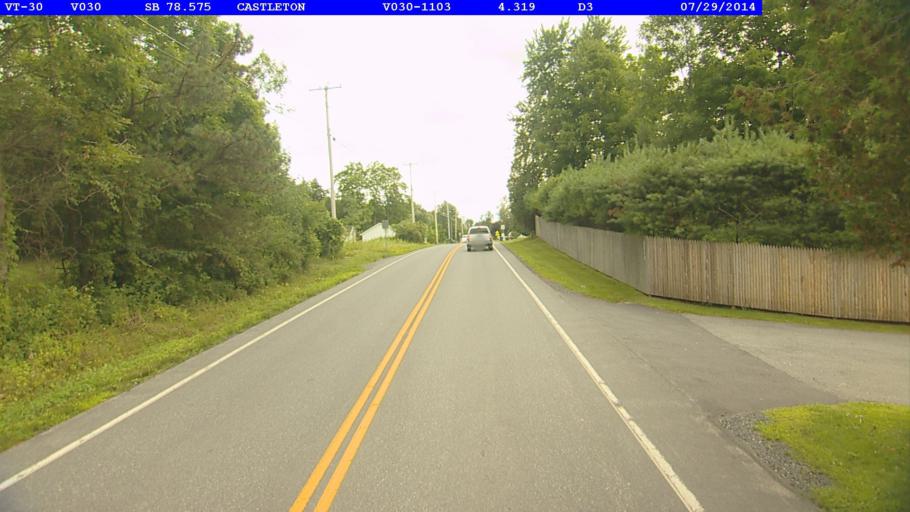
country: US
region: Vermont
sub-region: Rutland County
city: Castleton
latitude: 43.6479
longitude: -73.1964
